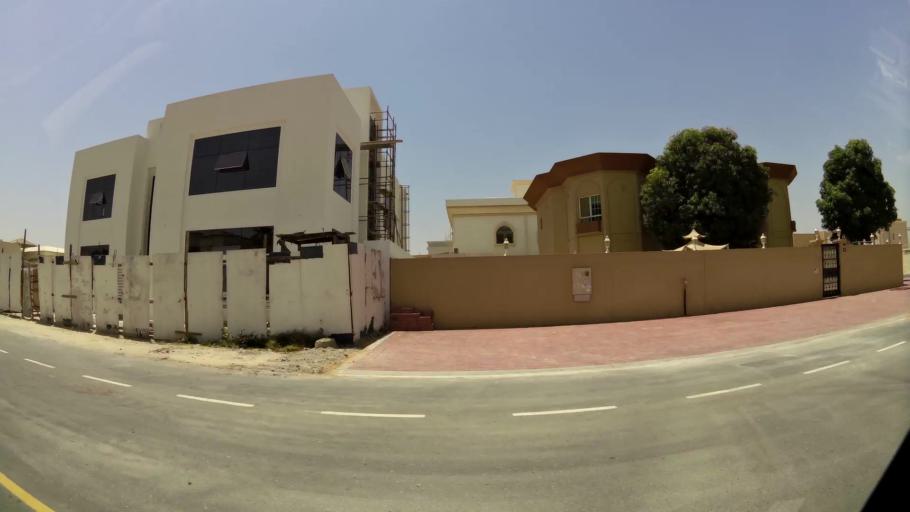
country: AE
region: Dubai
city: Dubai
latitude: 25.0868
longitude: 55.2120
